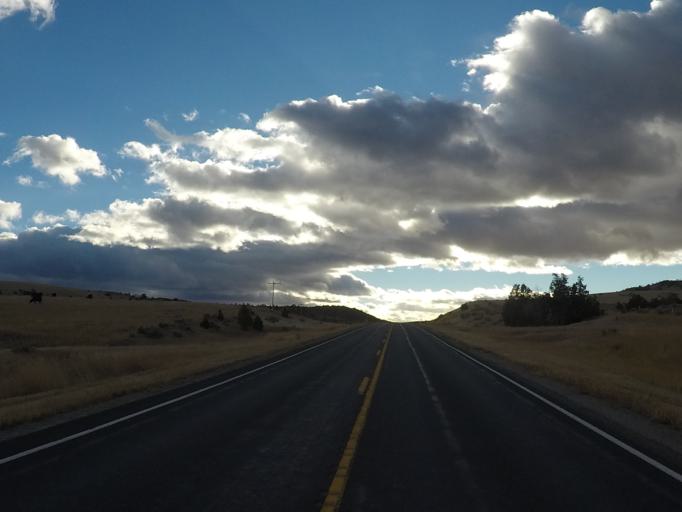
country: US
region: Montana
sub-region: Jefferson County
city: Whitehall
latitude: 45.9115
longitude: -111.9393
